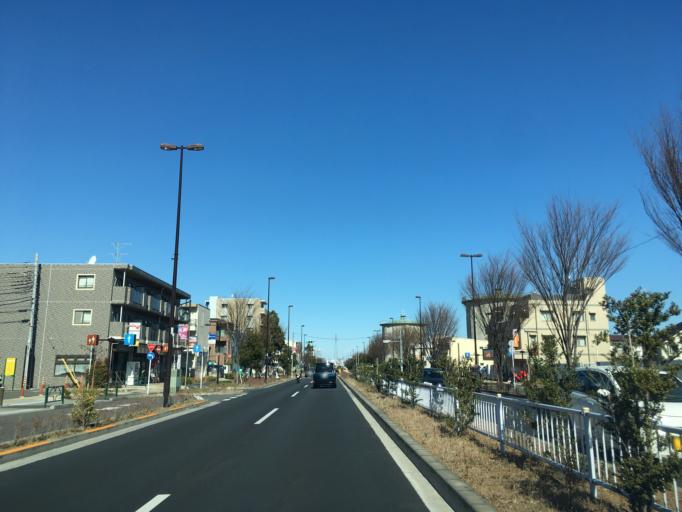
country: JP
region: Tokyo
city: Mitaka-shi
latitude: 35.6851
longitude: 139.5498
